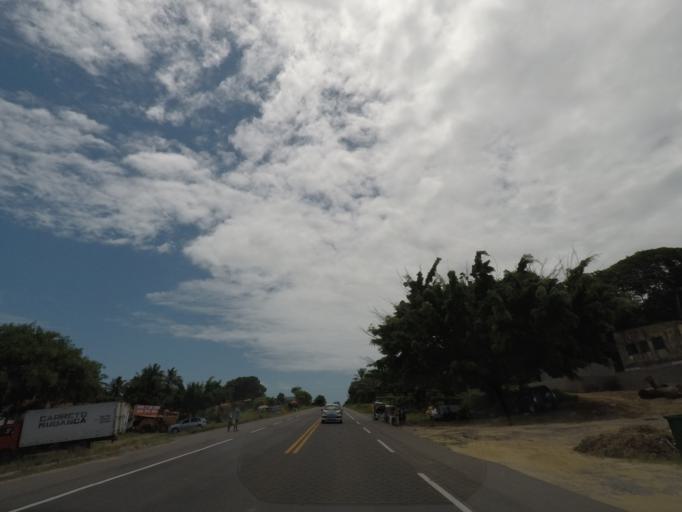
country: BR
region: Bahia
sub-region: Itaparica
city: Itaparica
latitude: -12.9548
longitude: -38.6323
